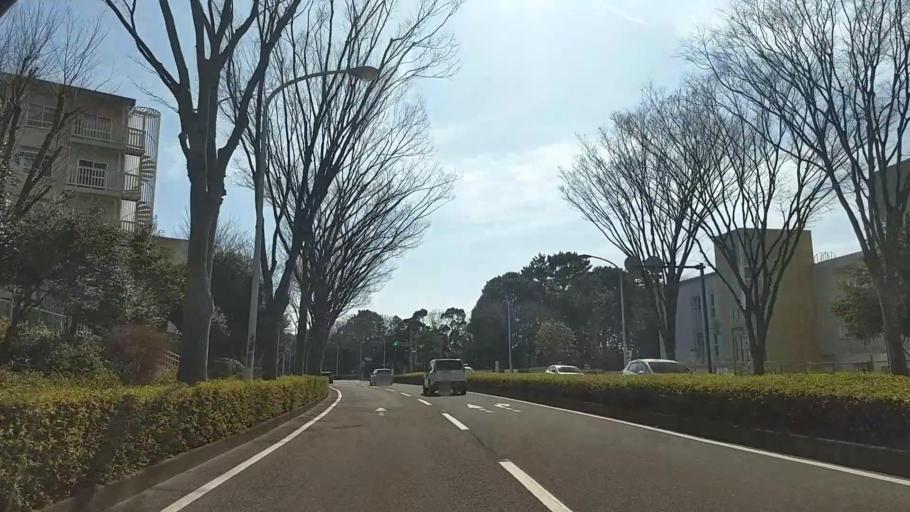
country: JP
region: Kanagawa
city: Fujisawa
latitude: 35.3572
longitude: 139.4430
